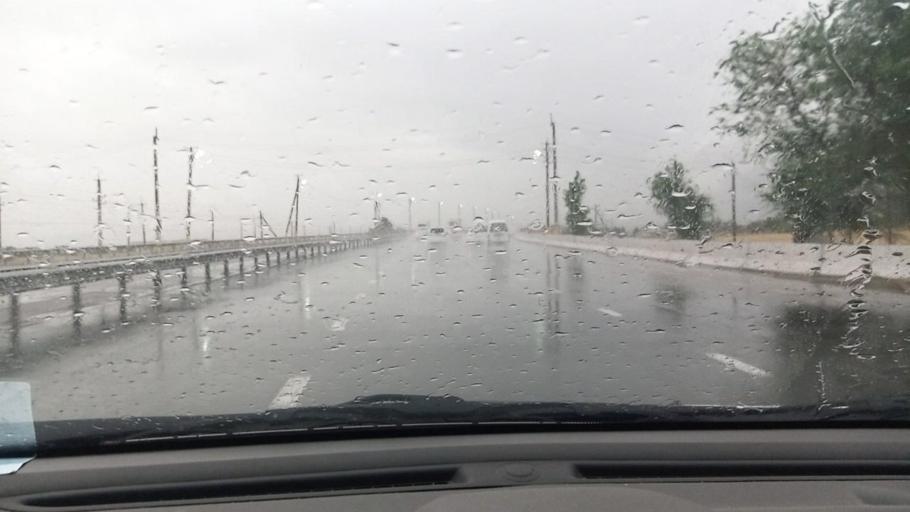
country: UZ
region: Toshkent
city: Ohangaron
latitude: 40.9283
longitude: 69.5961
